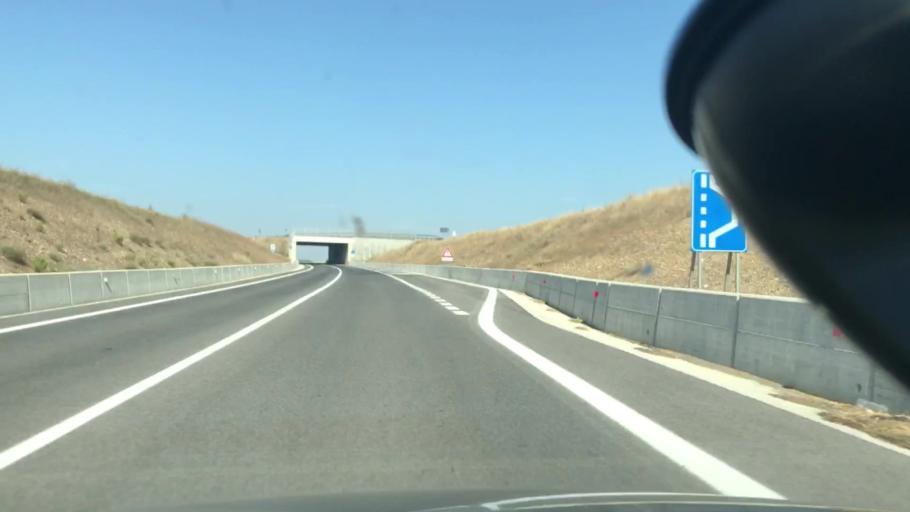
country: IT
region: Basilicate
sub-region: Provincia di Potenza
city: Palazzo San Gervasio
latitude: 40.9682
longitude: 16.0047
